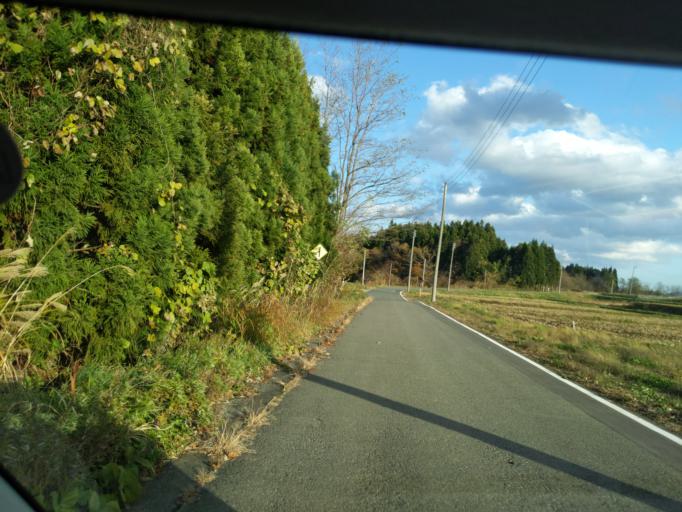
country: JP
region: Iwate
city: Mizusawa
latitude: 39.1193
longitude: 140.9950
